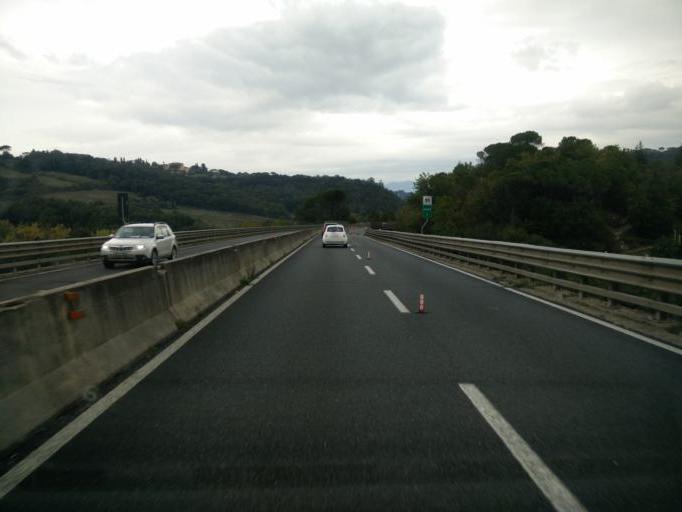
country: IT
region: Tuscany
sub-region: Province of Florence
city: San Casciano in Val di Pesa
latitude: 43.6752
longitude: 11.2101
